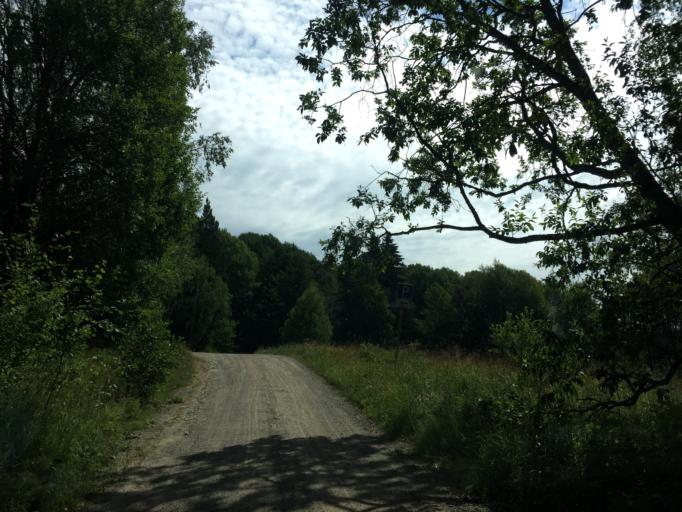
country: SE
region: Stockholm
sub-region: Botkyrka Kommun
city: Tumba
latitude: 59.1600
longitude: 17.8609
